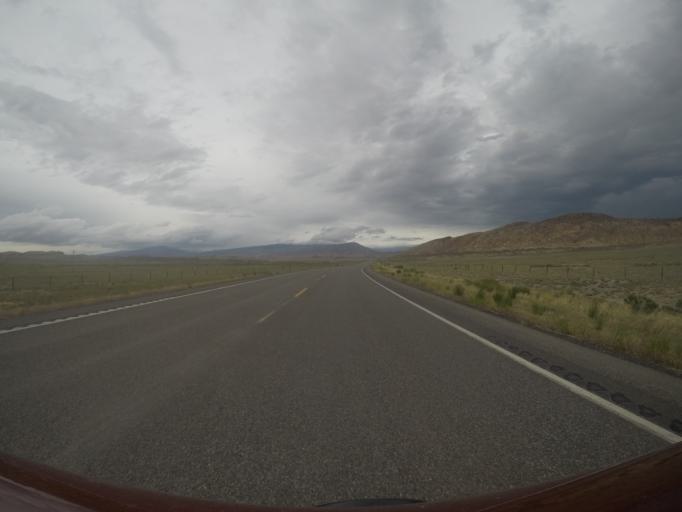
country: US
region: Wyoming
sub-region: Big Horn County
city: Lovell
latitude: 44.9266
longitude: -108.2994
